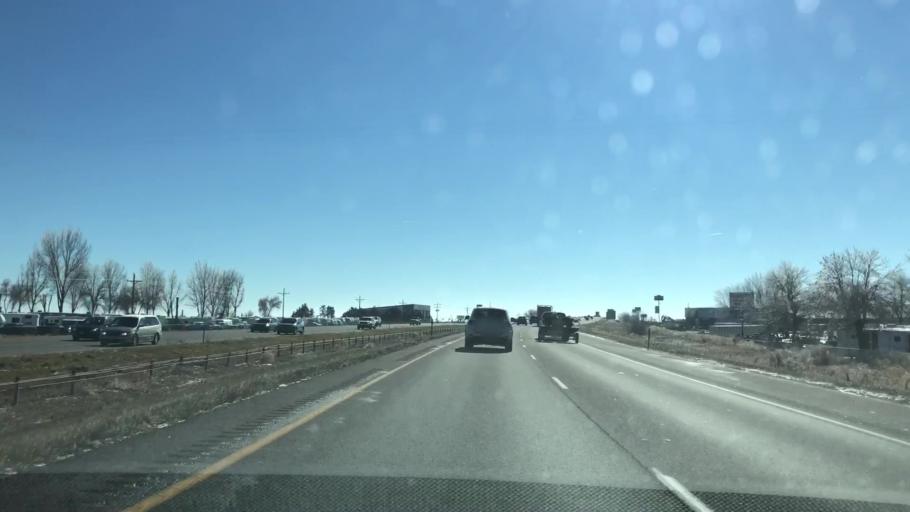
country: US
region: Colorado
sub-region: Weld County
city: Johnstown
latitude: 40.3560
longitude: -104.9824
